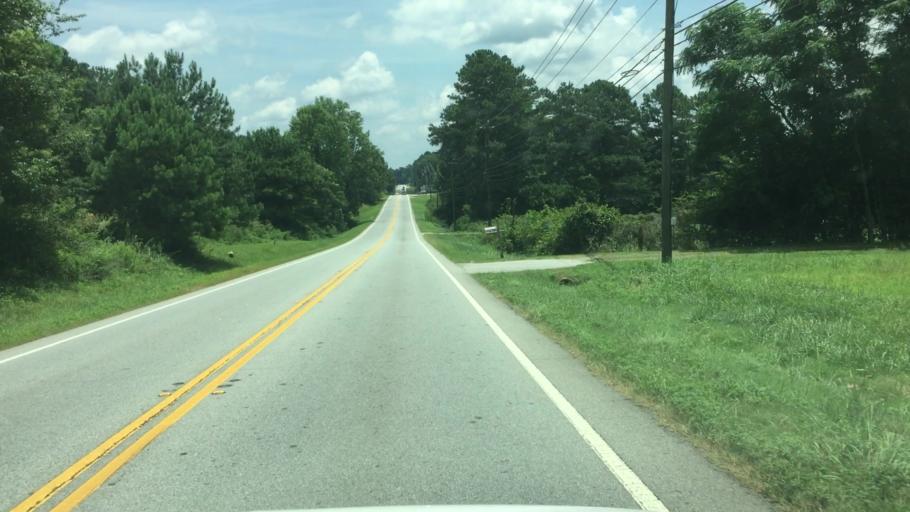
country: US
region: Georgia
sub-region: Barrow County
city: Auburn
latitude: 33.9988
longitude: -83.7940
